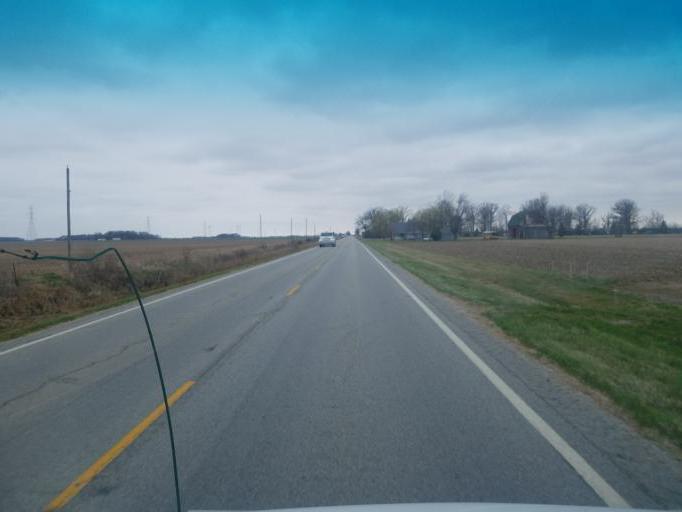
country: US
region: Ohio
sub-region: Van Wert County
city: Van Wert
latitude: 40.9321
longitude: -84.4660
